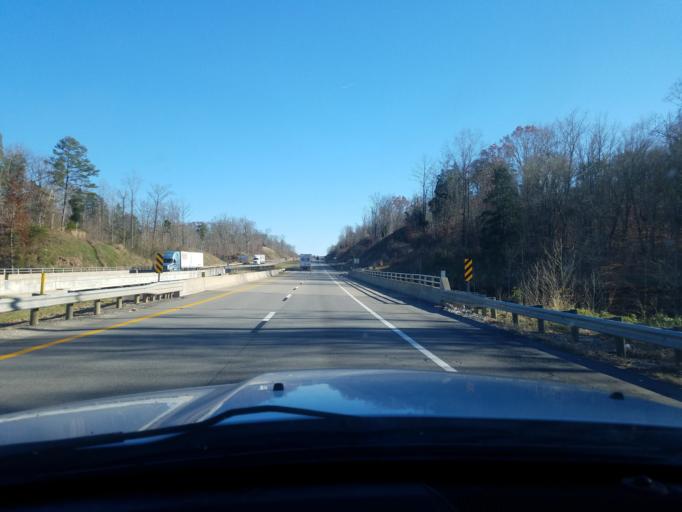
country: US
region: West Virginia
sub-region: Putnam County
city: Eleanor
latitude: 38.5461
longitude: -81.9741
